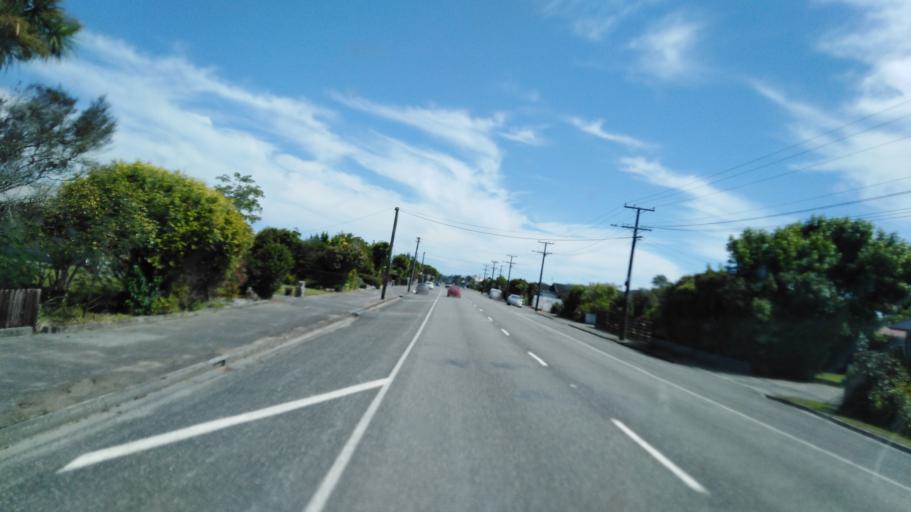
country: NZ
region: West Coast
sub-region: Buller District
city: Westport
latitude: -41.7536
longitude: 171.6135
